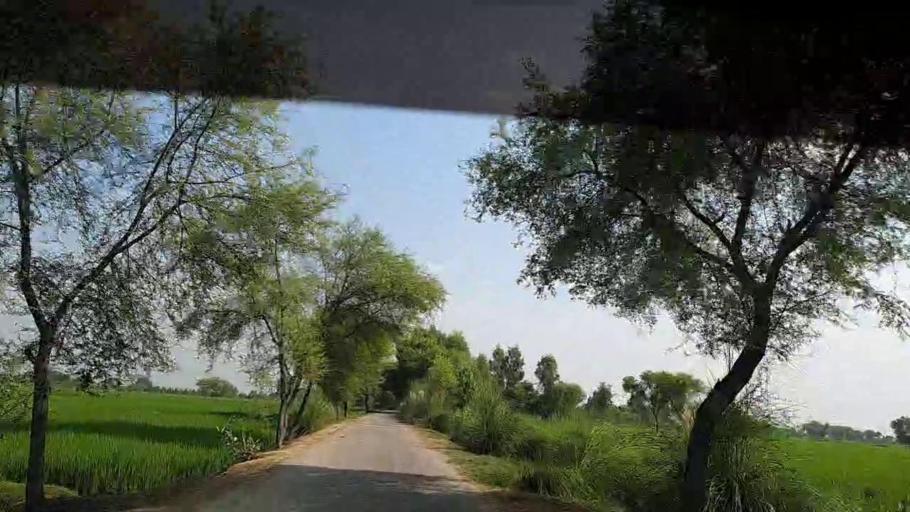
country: PK
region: Sindh
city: Shikarpur
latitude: 28.0948
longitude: 68.6757
